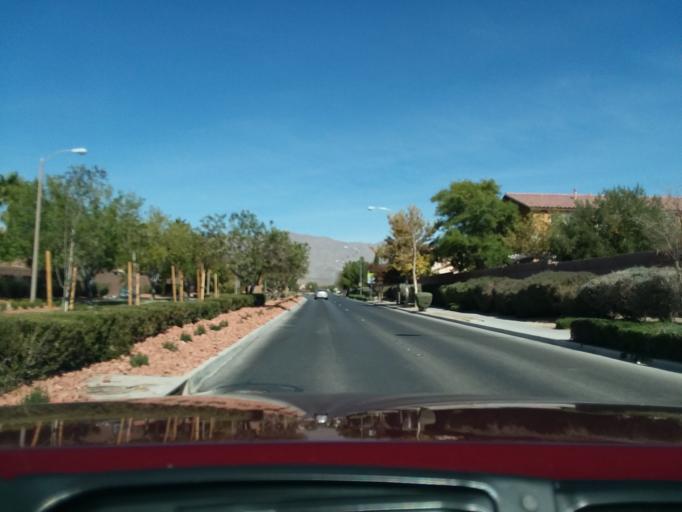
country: US
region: Nevada
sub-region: Clark County
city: North Las Vegas
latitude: 36.2824
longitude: -115.1711
